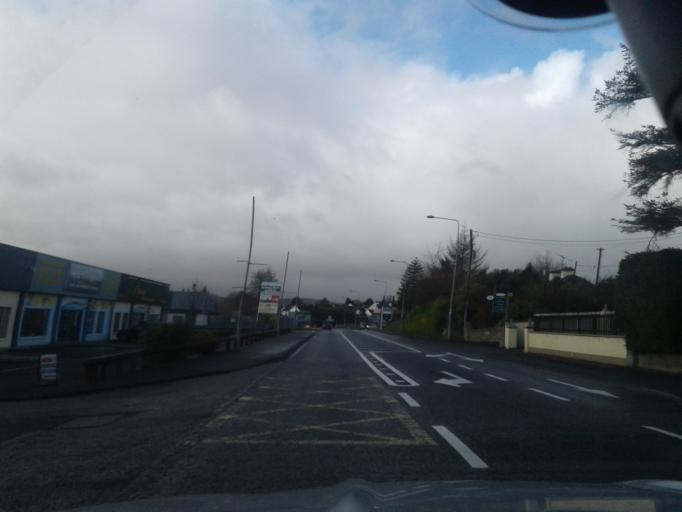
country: IE
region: Ulster
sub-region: County Donegal
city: Letterkenny
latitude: 54.9571
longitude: -7.7065
